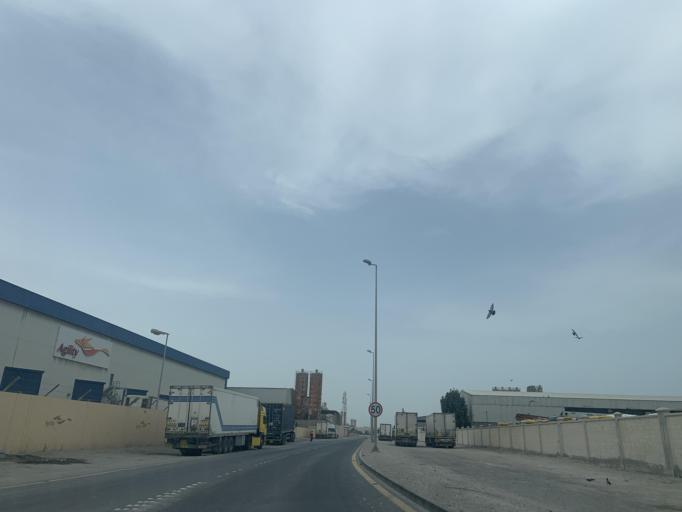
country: BH
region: Muharraq
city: Al Hadd
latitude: 26.2044
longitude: 50.6631
